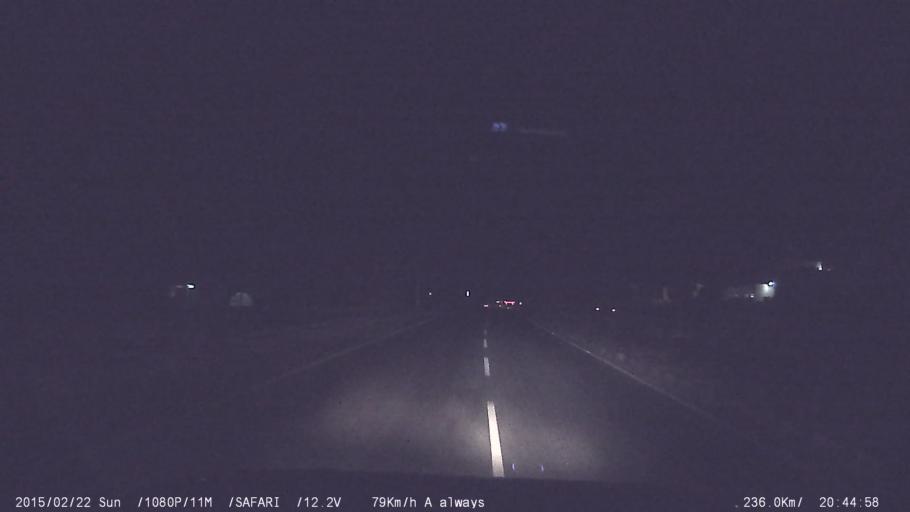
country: IN
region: Tamil Nadu
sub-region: Dindigul
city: Vedasandur
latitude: 10.4630
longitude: 77.9470
